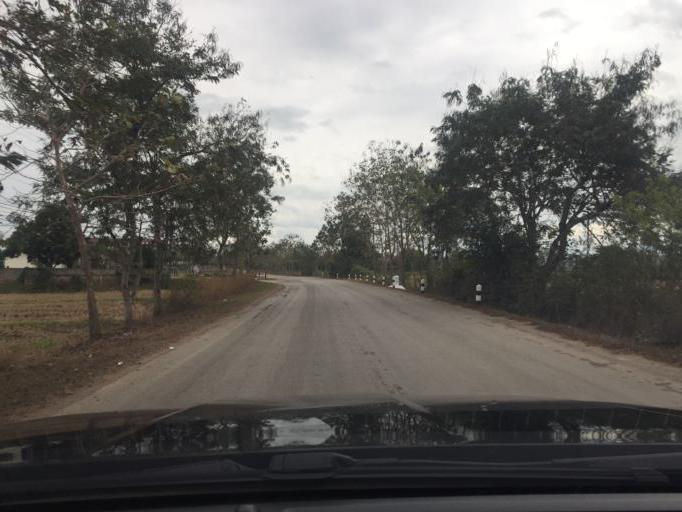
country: TH
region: Phayao
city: Pong
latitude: 19.1667
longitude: 100.2967
